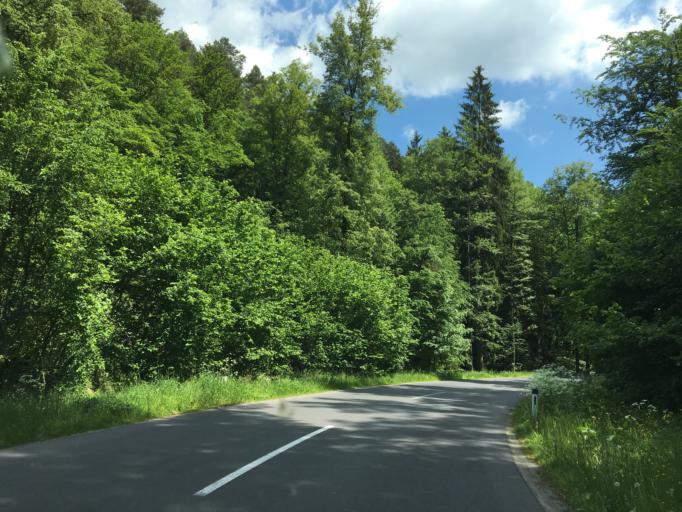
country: AT
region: Upper Austria
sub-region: Politischer Bezirk Perg
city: Perg
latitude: 48.3117
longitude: 14.6114
